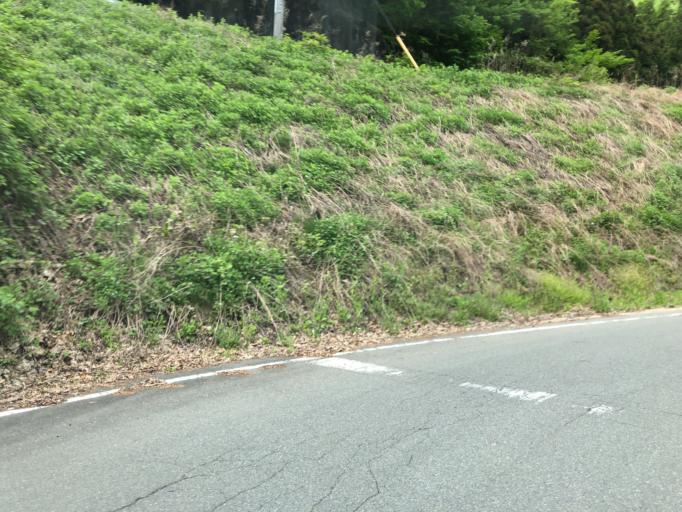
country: JP
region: Miyagi
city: Marumori
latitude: 37.7208
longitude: 140.7855
